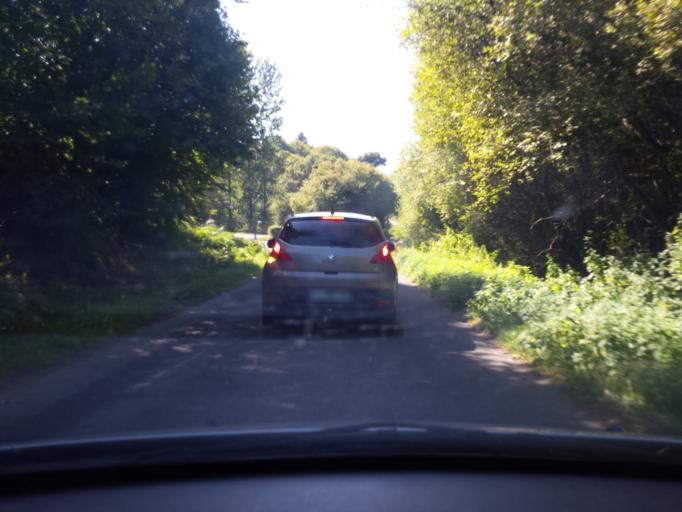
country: FR
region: Brittany
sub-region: Departement des Cotes-d'Armor
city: Plounevez-Quintin
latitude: 48.3428
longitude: -3.2470
